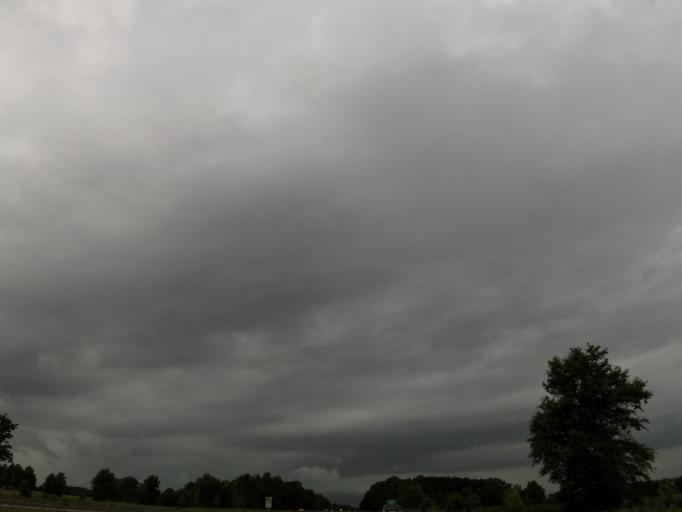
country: US
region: Illinois
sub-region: Clinton County
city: Wamac
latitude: 38.3874
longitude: -89.1454
